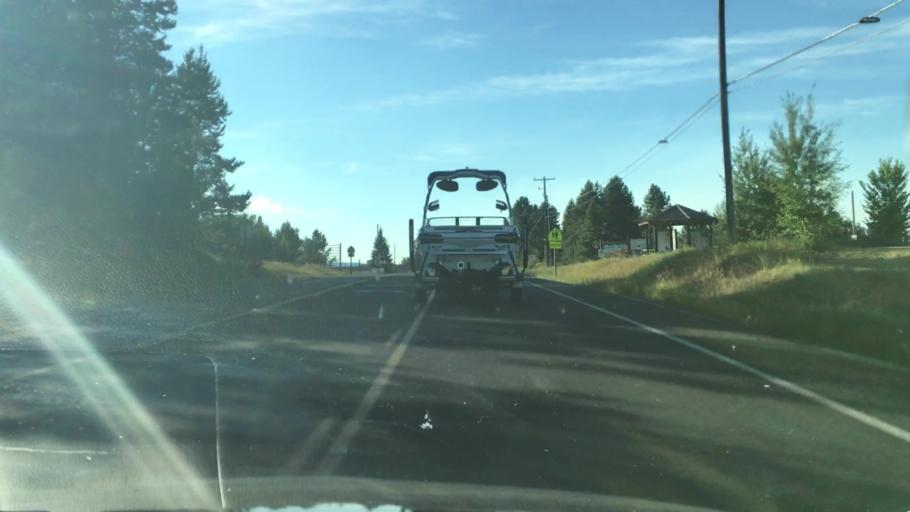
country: US
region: Idaho
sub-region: Valley County
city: McCall
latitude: 44.7279
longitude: -116.0754
